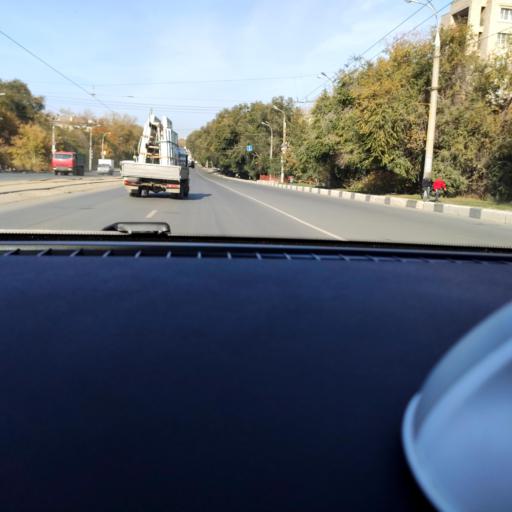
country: RU
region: Samara
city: Samara
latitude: 53.2144
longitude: 50.2691
